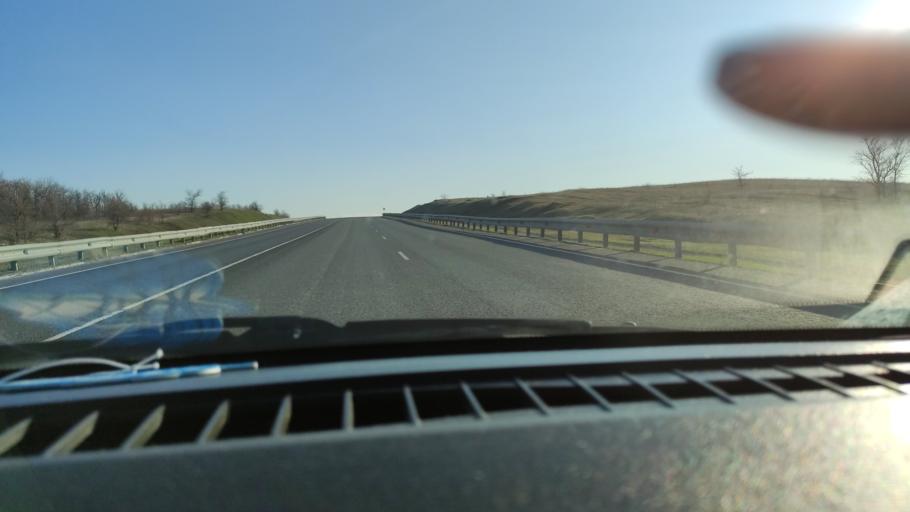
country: RU
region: Saratov
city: Alekseyevka
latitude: 52.2200
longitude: 47.8958
